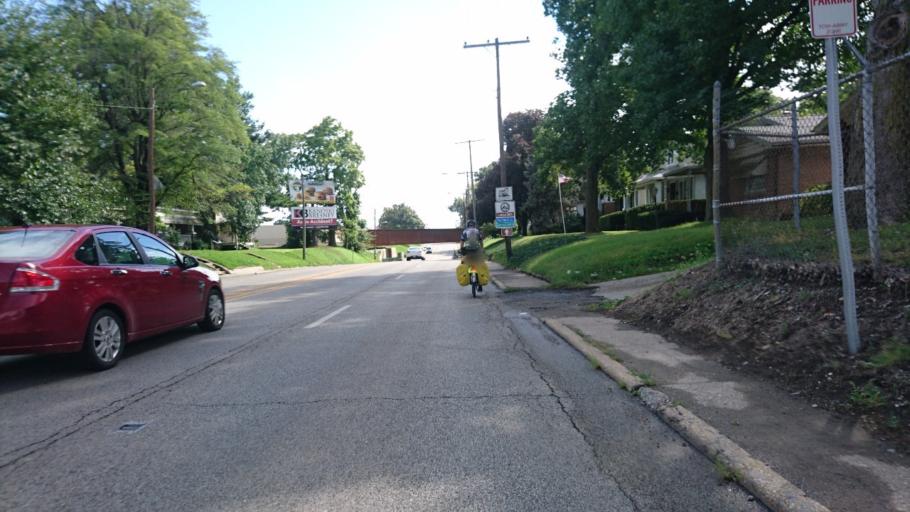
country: US
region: Illinois
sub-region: Sangamon County
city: Springfield
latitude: 39.8222
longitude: -89.6433
